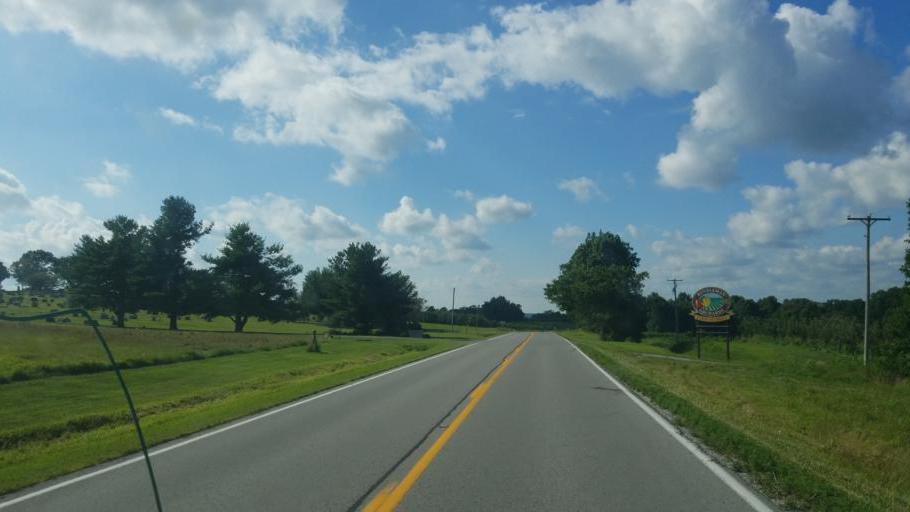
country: US
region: Illinois
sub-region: Union County
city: Cobden
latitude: 37.5832
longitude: -89.3221
